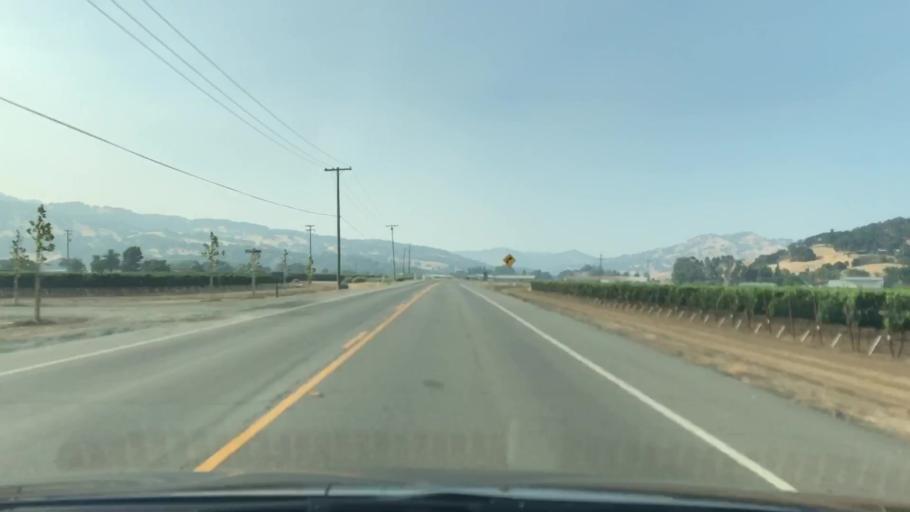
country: US
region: California
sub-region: Solano County
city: Green Valley
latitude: 38.2828
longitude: -122.1173
